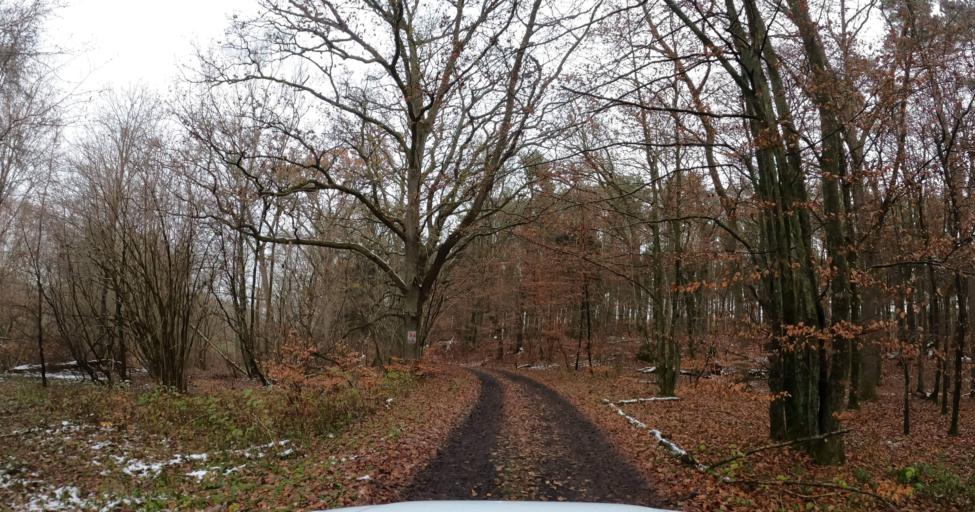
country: PL
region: West Pomeranian Voivodeship
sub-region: Powiat swidwinski
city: Rabino
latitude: 53.9123
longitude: 15.8673
